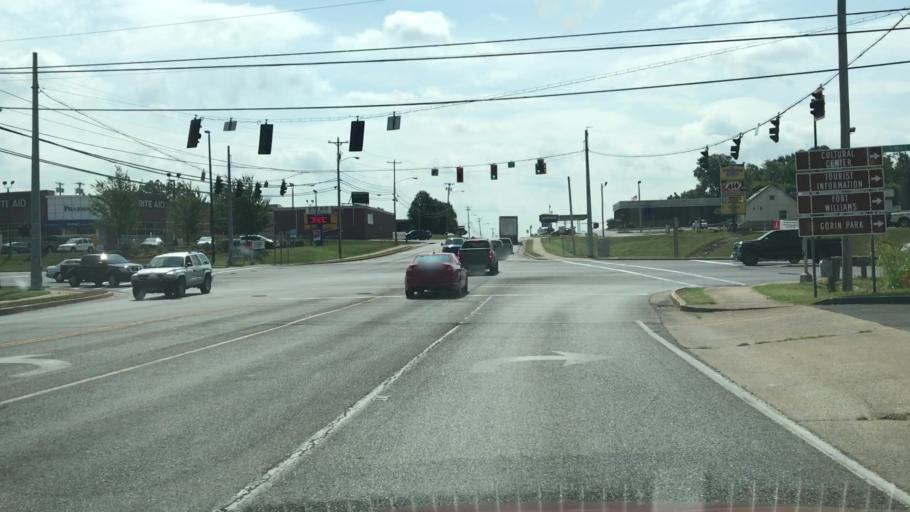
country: US
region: Kentucky
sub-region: Barren County
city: Glasgow
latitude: 37.0098
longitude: -85.9221
